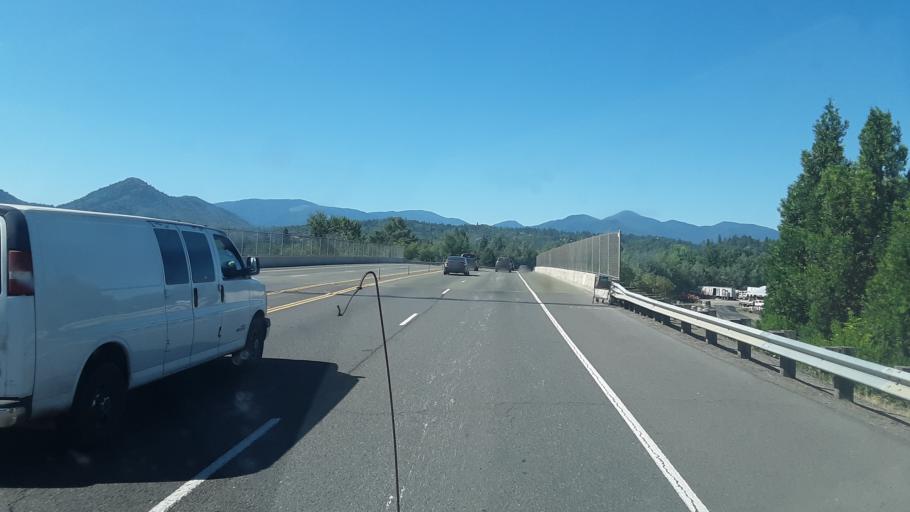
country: US
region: Oregon
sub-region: Josephine County
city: Fruitdale
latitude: 42.4353
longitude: -123.3120
